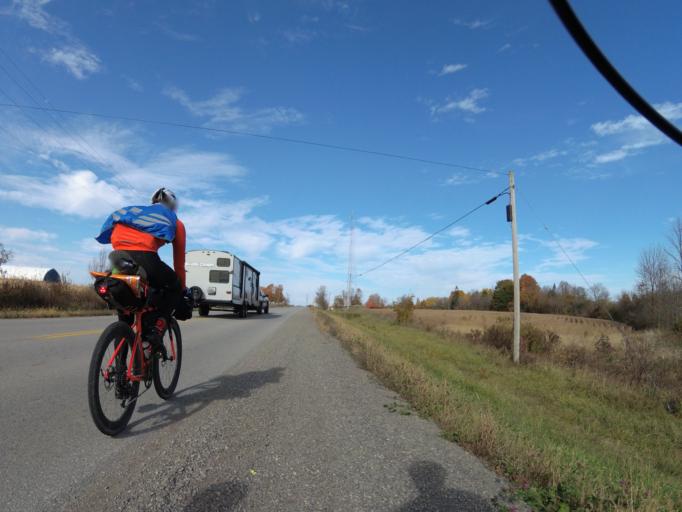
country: CA
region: Ontario
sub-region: Lanark County
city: Smiths Falls
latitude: 44.8892
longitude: -76.0085
